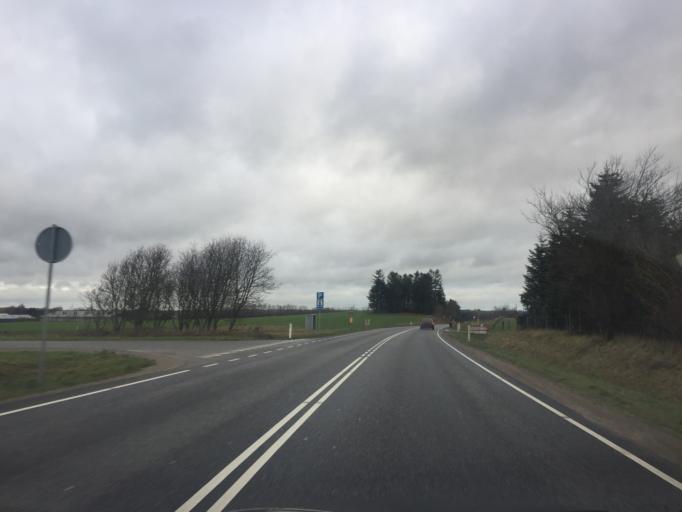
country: DK
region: Zealand
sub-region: Soro Kommune
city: Stenlille
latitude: 55.5195
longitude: 11.5809
